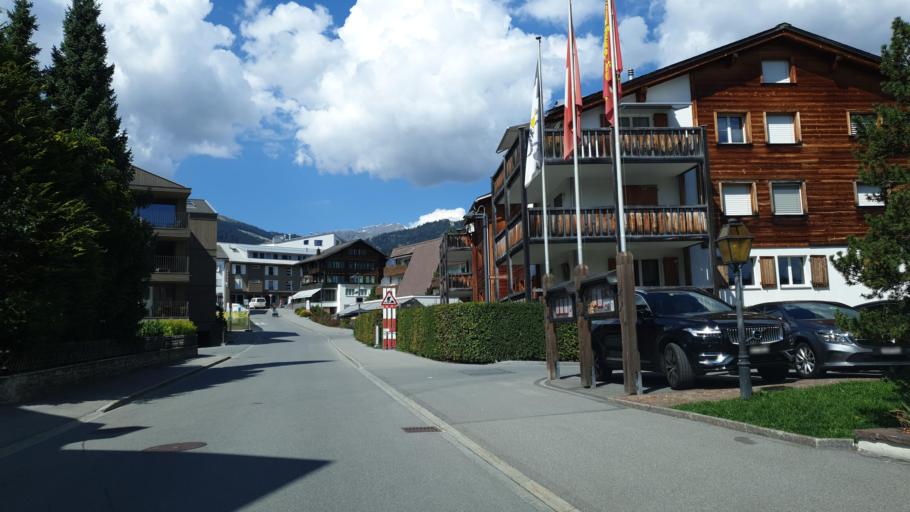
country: CH
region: Grisons
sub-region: Imboden District
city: Flims
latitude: 46.8280
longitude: 9.2896
